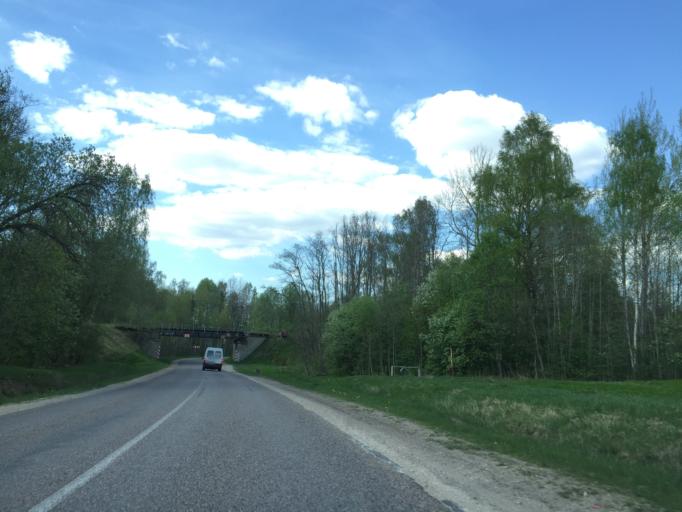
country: LV
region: Limbazu Rajons
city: Limbazi
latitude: 57.4738
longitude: 24.7117
